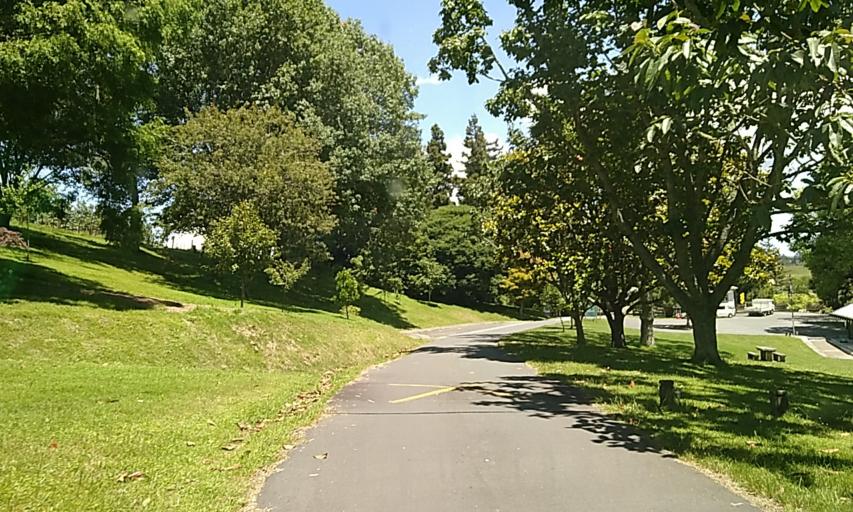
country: NZ
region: Bay of Plenty
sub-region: Tauranga City
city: Tauranga
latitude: -37.8089
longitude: 176.0455
